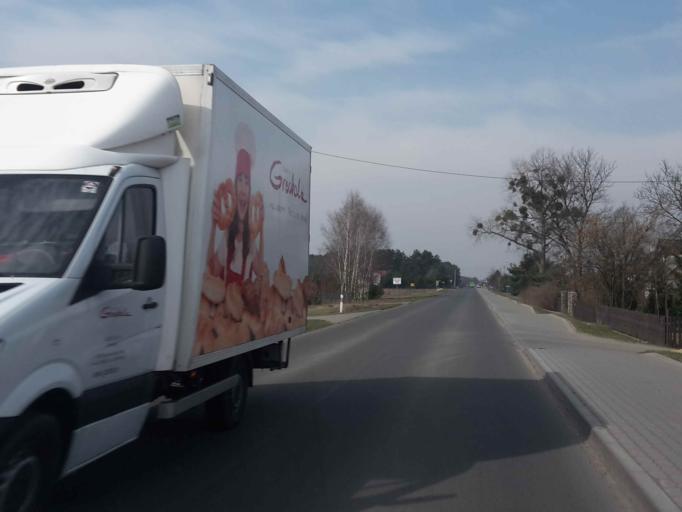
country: PL
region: Kujawsko-Pomorskie
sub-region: Powiat nakielski
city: Szubin
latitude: 53.0745
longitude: 17.8052
